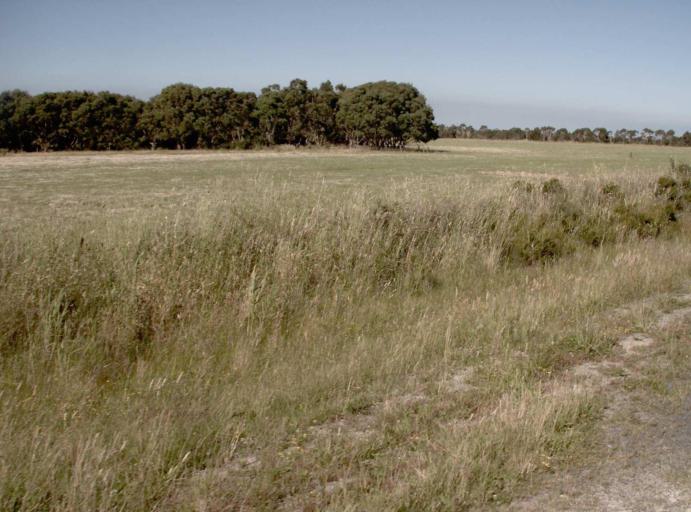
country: AU
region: Victoria
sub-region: Latrobe
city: Morwell
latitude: -38.6329
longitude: 146.5676
